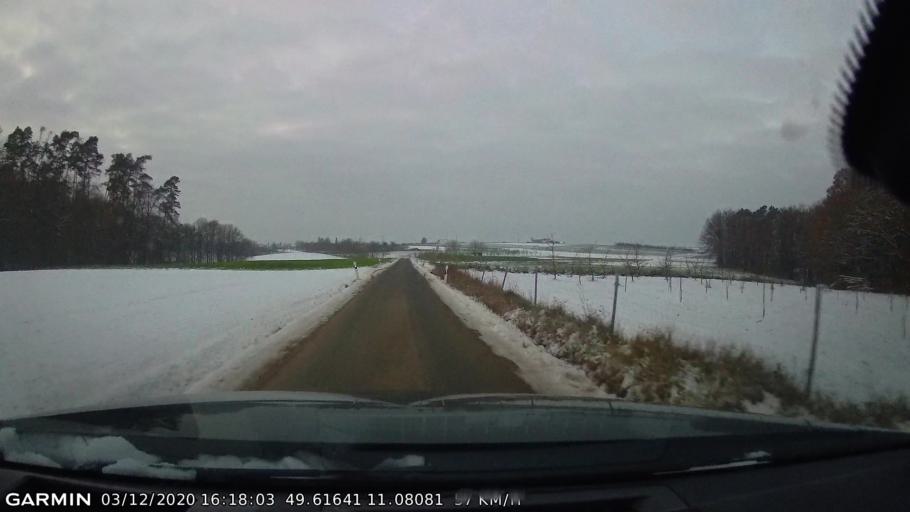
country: DE
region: Bavaria
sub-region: Regierungsbezirk Mittelfranken
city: Marloffstein
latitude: 49.6166
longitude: 11.0804
